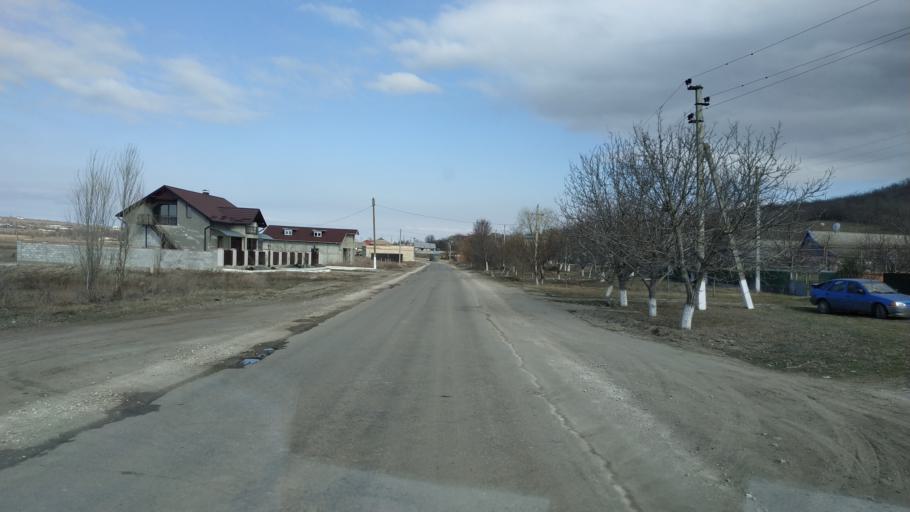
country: MD
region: Causeni
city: Causeni
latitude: 46.6401
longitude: 29.3824
